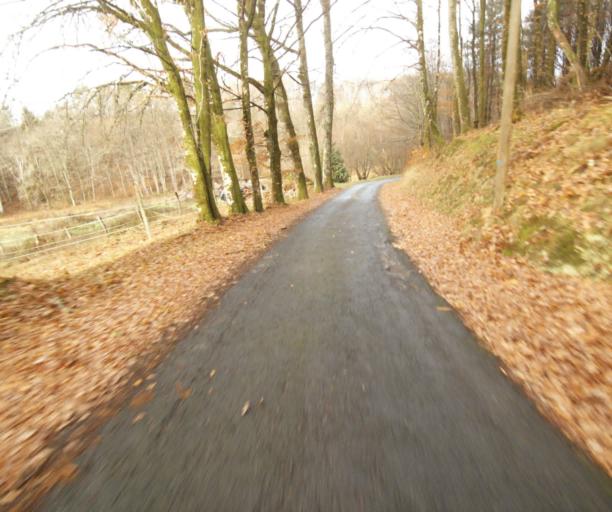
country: FR
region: Limousin
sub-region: Departement de la Correze
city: Saint-Mexant
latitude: 45.2544
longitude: 1.6434
